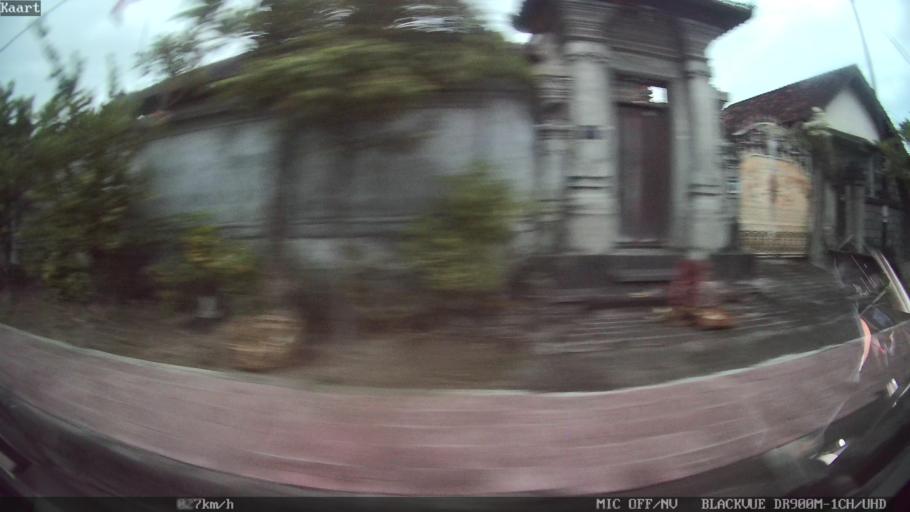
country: ID
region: Bali
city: Banjar Pasekan
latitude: -8.6215
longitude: 115.2841
